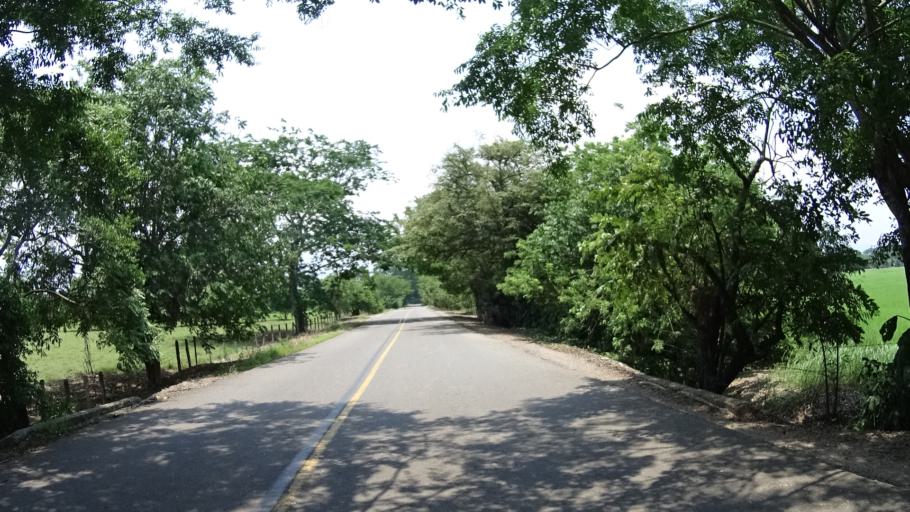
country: CO
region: Cundinamarca
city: Puerto Salgar
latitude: 5.4940
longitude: -74.6829
